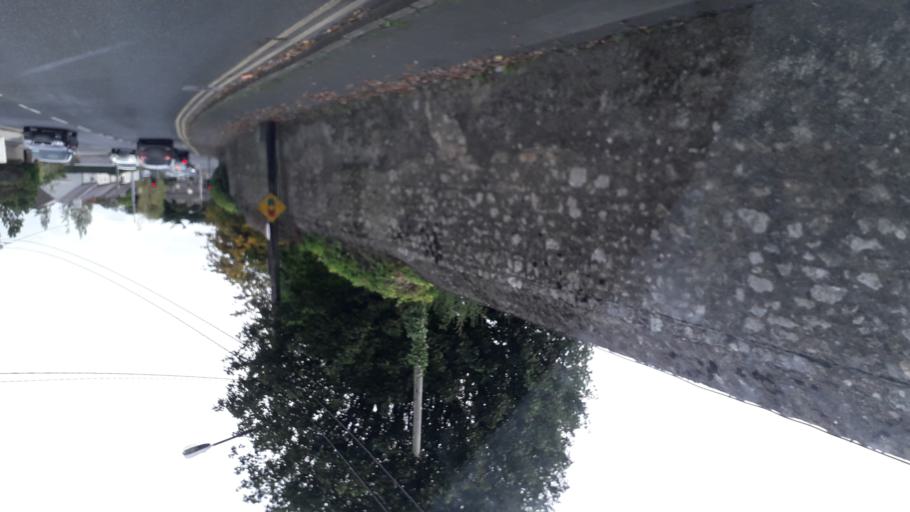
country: IE
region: Leinster
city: Cabinteely
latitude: 53.2671
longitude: -6.1642
